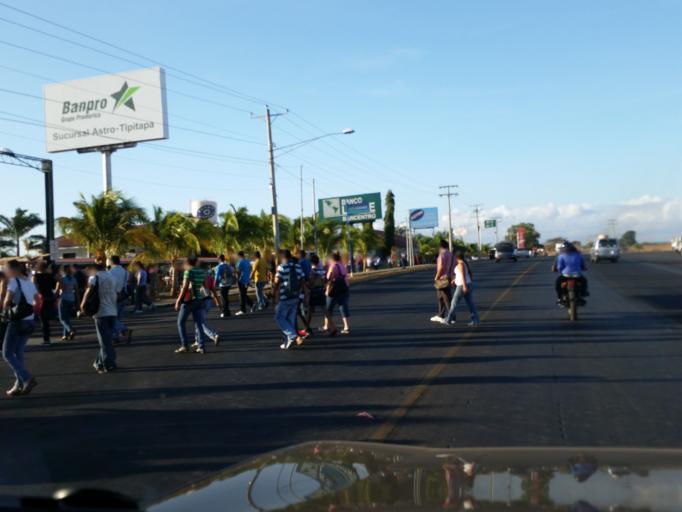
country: NI
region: Managua
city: Tipitapa
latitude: 12.1655
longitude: -86.0930
